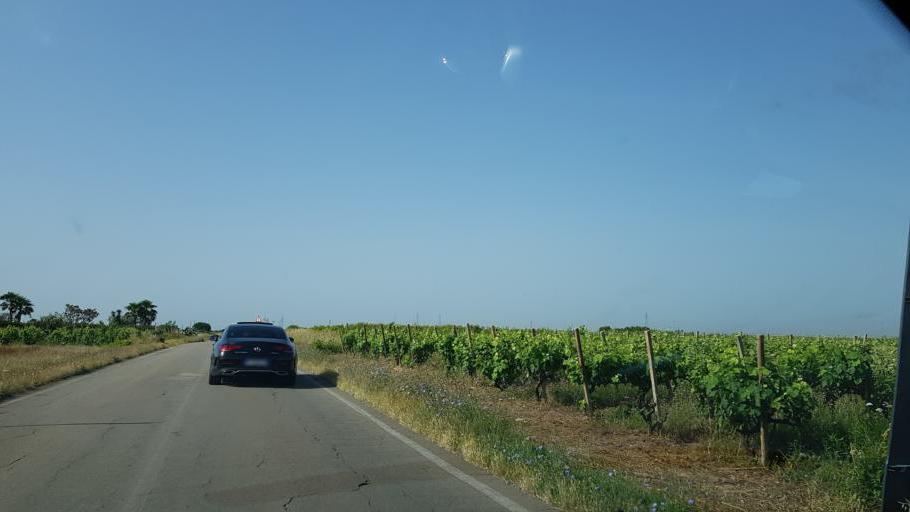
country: IT
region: Apulia
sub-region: Provincia di Brindisi
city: San Pancrazio Salentino
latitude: 40.3998
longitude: 17.8352
